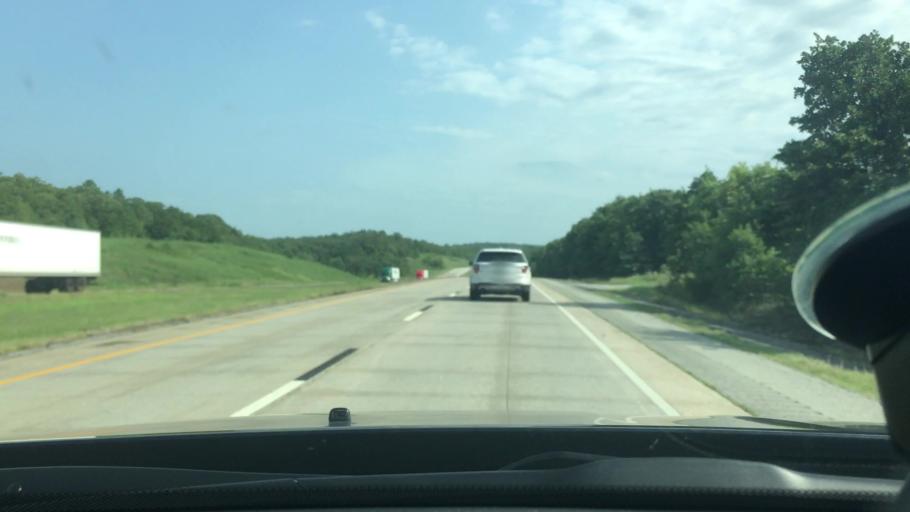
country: US
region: Oklahoma
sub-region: Atoka County
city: Atoka
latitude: 34.4461
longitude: -96.0714
